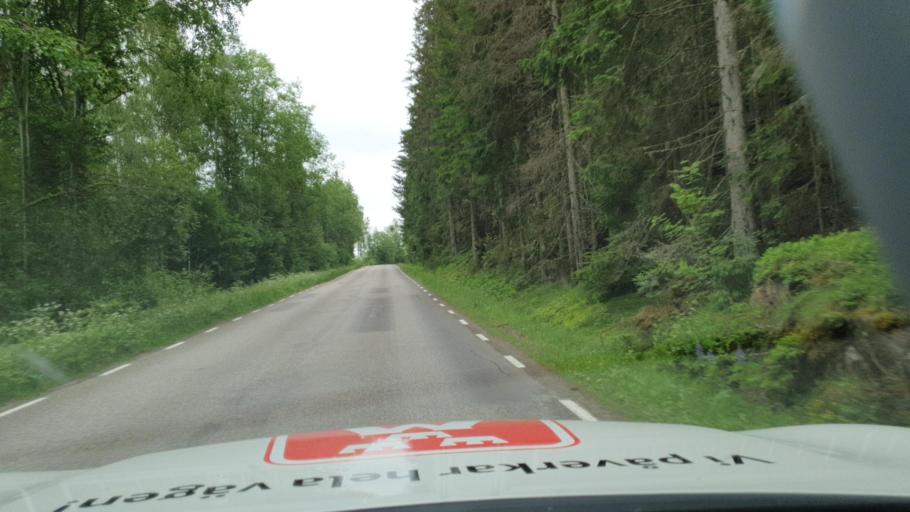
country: SE
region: Vaermland
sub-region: Kils Kommun
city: Kil
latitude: 59.6595
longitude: 13.3051
